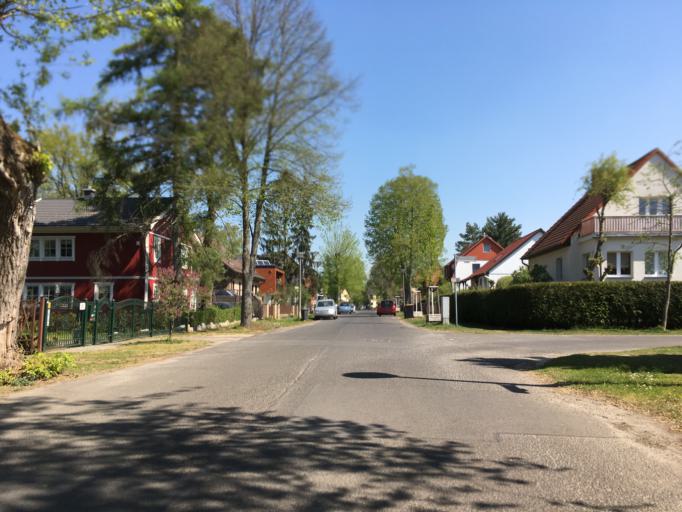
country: DE
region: Berlin
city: Buch
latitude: 52.6472
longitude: 13.5020
